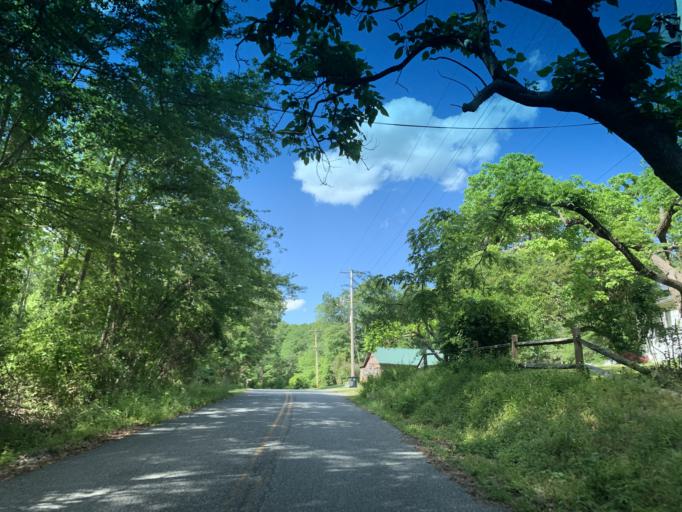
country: US
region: Maryland
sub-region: Cecil County
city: Charlestown
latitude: 39.5463
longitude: -75.9470
